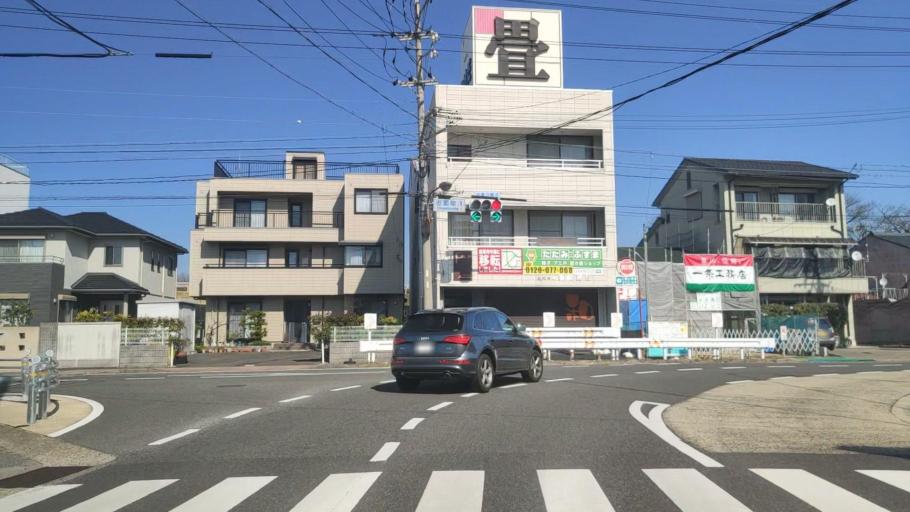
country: JP
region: Gifu
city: Gifu-shi
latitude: 35.4295
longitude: 136.7591
